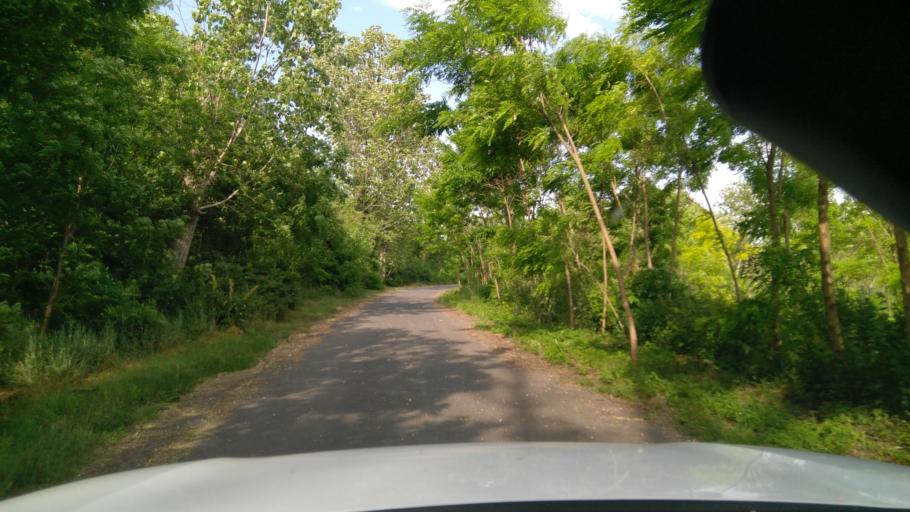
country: HU
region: Bekes
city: Bekes
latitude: 46.7075
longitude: 21.1673
